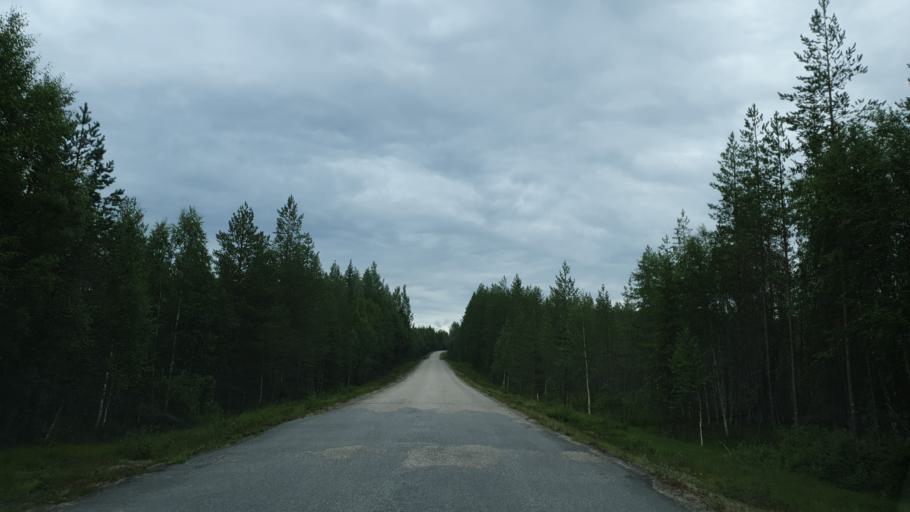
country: FI
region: Kainuu
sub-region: Kehys-Kainuu
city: Kuhmo
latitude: 64.3256
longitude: 29.4227
